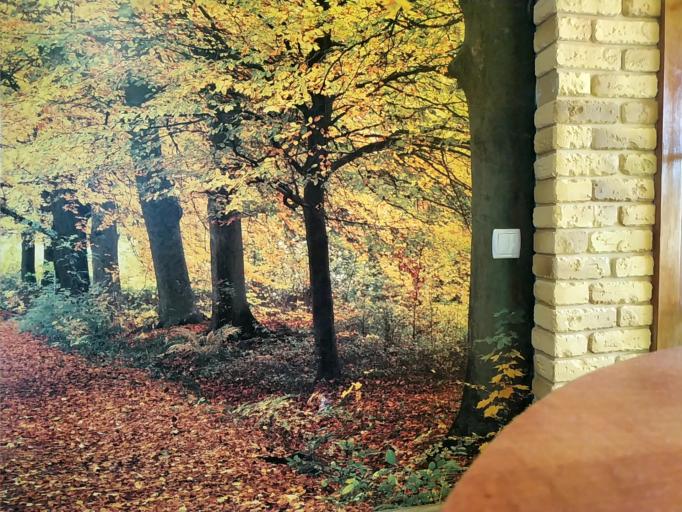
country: RU
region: Novgorod
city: Sol'tsy
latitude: 57.9073
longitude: 30.2026
